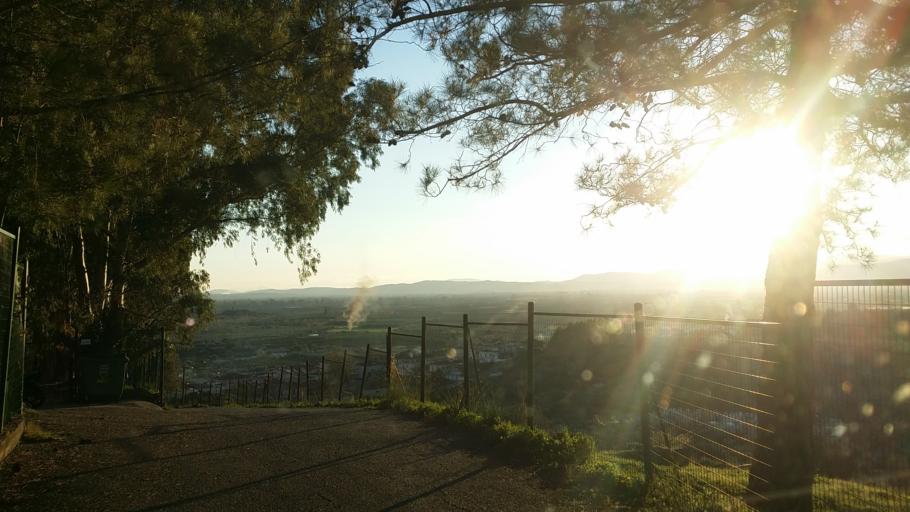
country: GR
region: West Greece
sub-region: Nomos Aitolias kai Akarnanias
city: Neapolis
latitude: 38.6714
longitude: 21.3189
